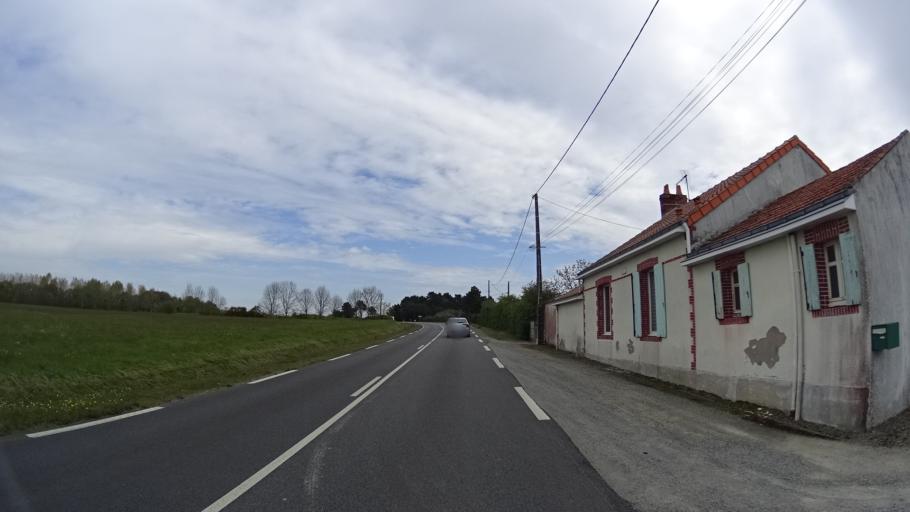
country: FR
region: Pays de la Loire
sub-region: Departement de la Loire-Atlantique
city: Bourgneuf-en-Retz
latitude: 47.0455
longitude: -1.9420
